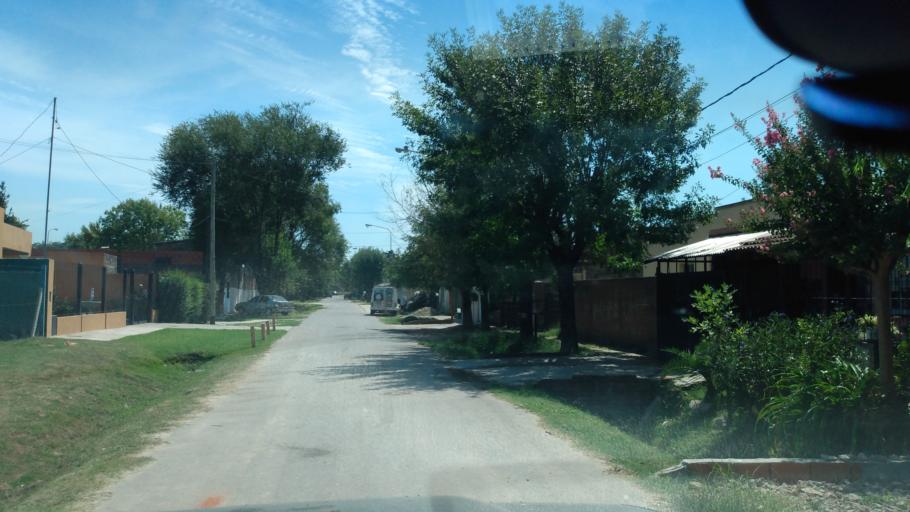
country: AR
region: Buenos Aires
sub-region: Partido de Lujan
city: Lujan
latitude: -34.5530
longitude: -59.1198
